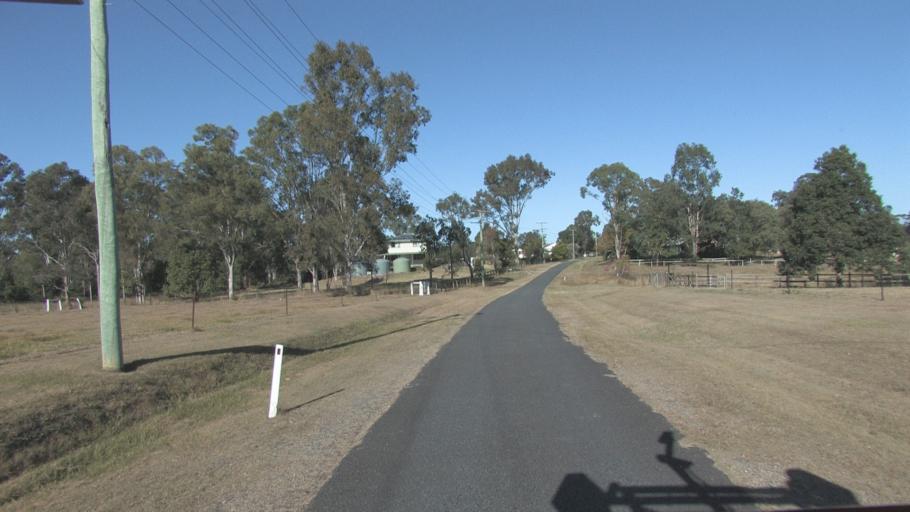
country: AU
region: Queensland
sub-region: Logan
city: Chambers Flat
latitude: -27.7581
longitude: 153.0536
